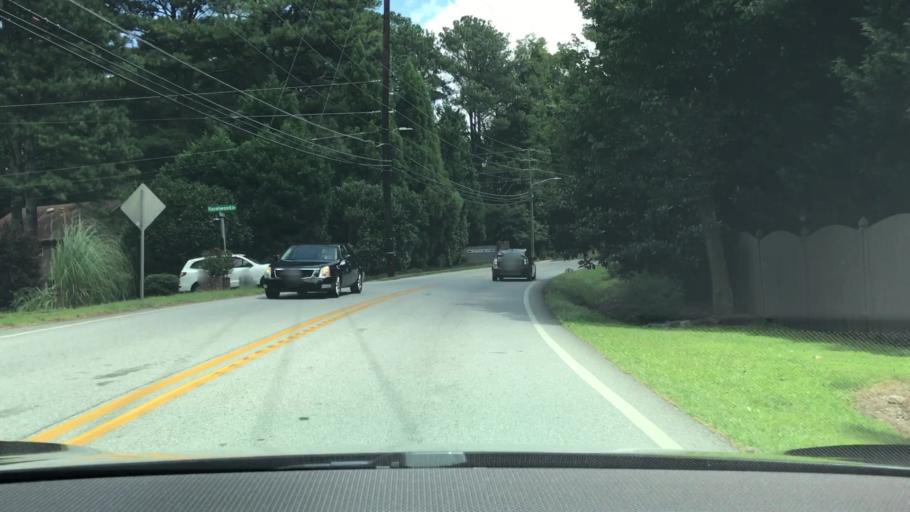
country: US
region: Georgia
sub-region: DeKalb County
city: Doraville
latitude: 33.8556
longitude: -84.2641
